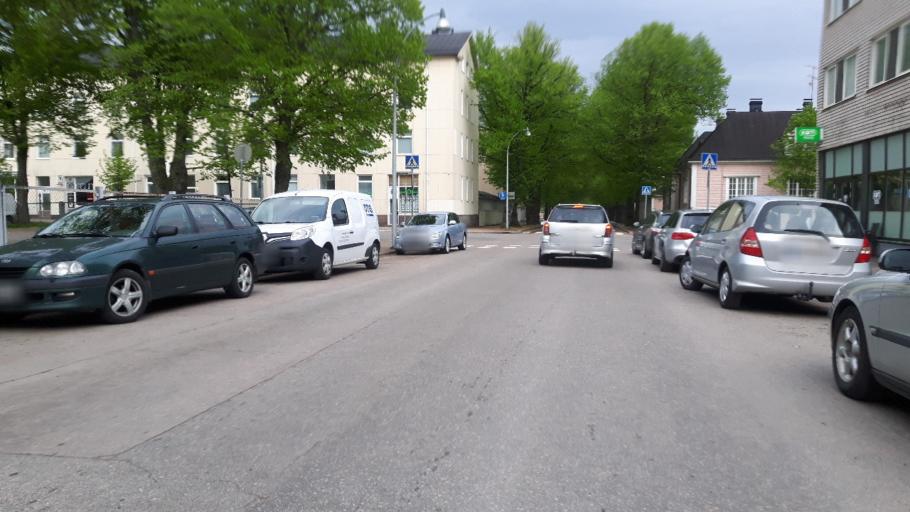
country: FI
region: Kymenlaakso
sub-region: Kotka-Hamina
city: Hamina
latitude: 60.5672
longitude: 27.1910
